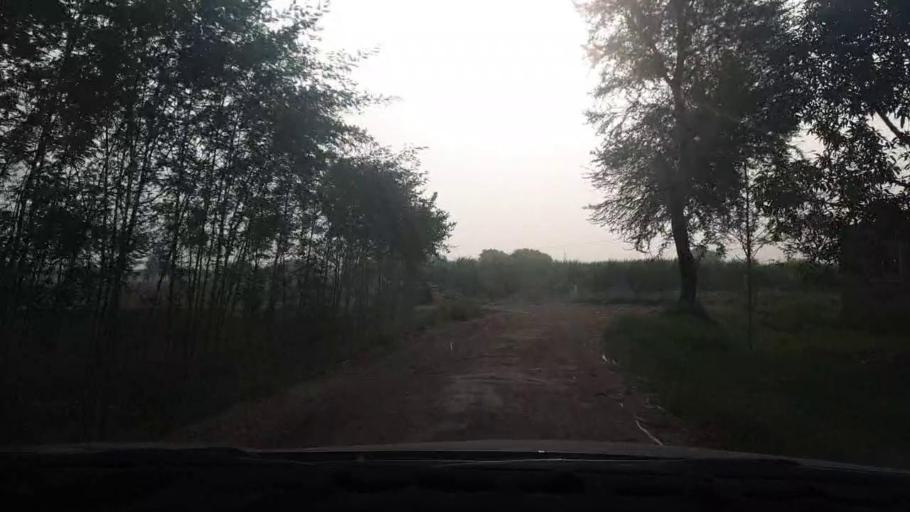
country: PK
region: Sindh
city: Matiari
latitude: 25.5828
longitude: 68.4575
